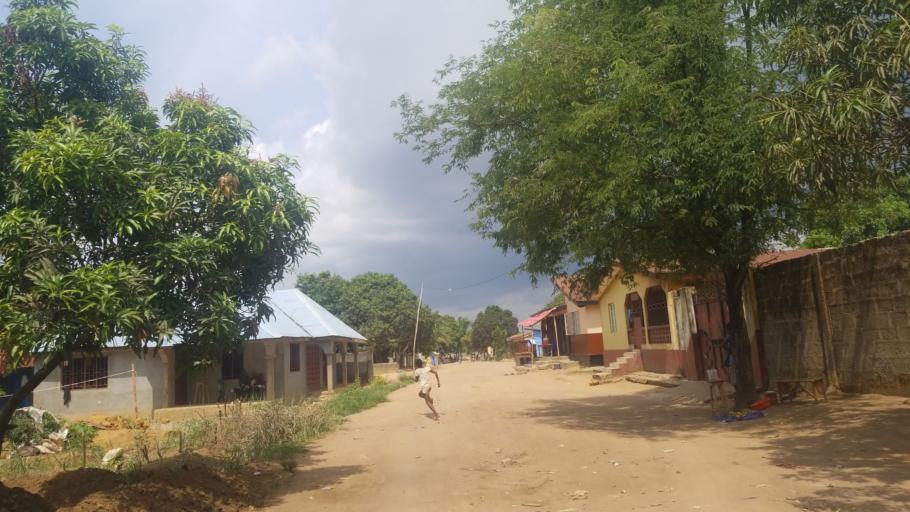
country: SL
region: Western Area
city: Waterloo
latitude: 8.3197
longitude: -13.0457
